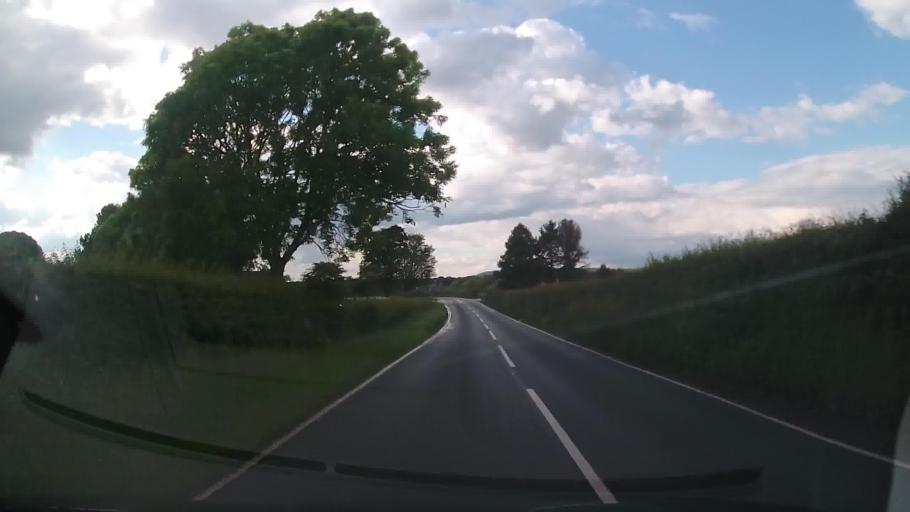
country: GB
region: England
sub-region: Shropshire
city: Withington
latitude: 52.6743
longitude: -2.6433
